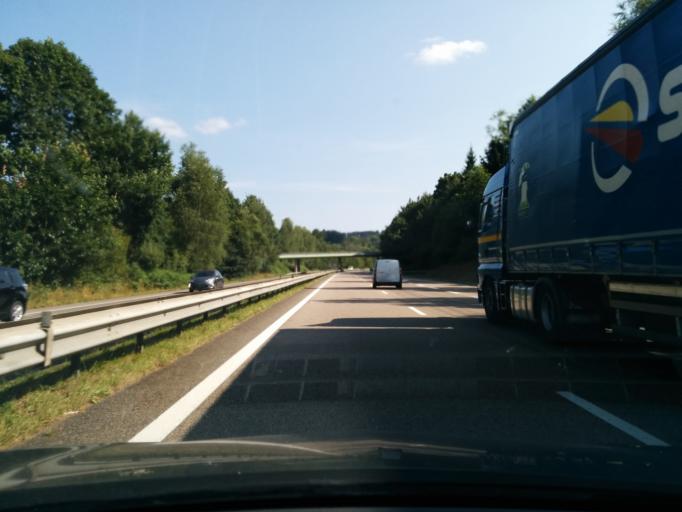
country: FR
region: Limousin
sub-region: Departement de la Haute-Vienne
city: Razes
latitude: 45.9852
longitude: 1.3254
